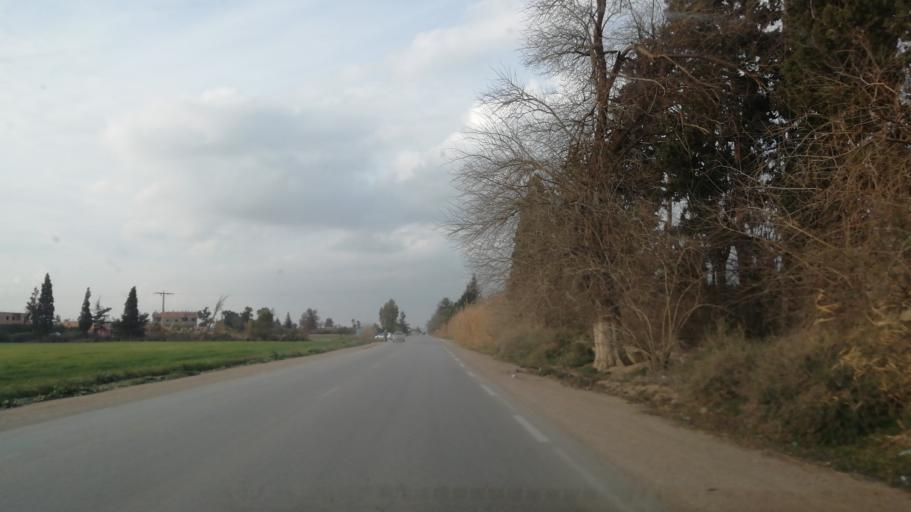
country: DZ
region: Mascara
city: Sig
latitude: 35.6795
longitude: -0.0095
